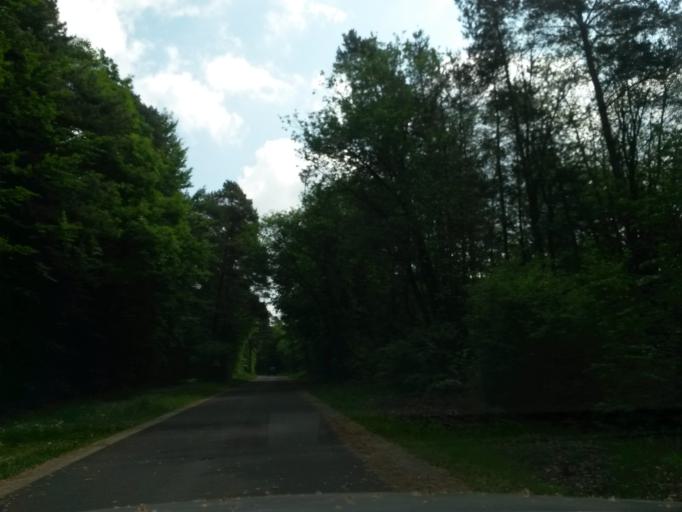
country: DE
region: Bavaria
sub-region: Regierungsbezirk Unterfranken
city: Nudlingen
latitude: 50.1995
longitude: 10.1077
